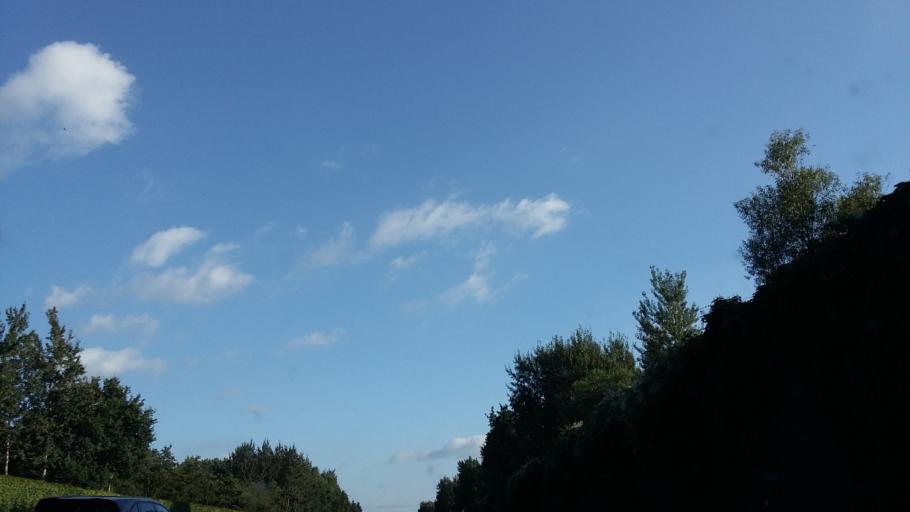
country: DE
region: Lower Saxony
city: Schiffdorf
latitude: 53.5351
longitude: 8.6207
